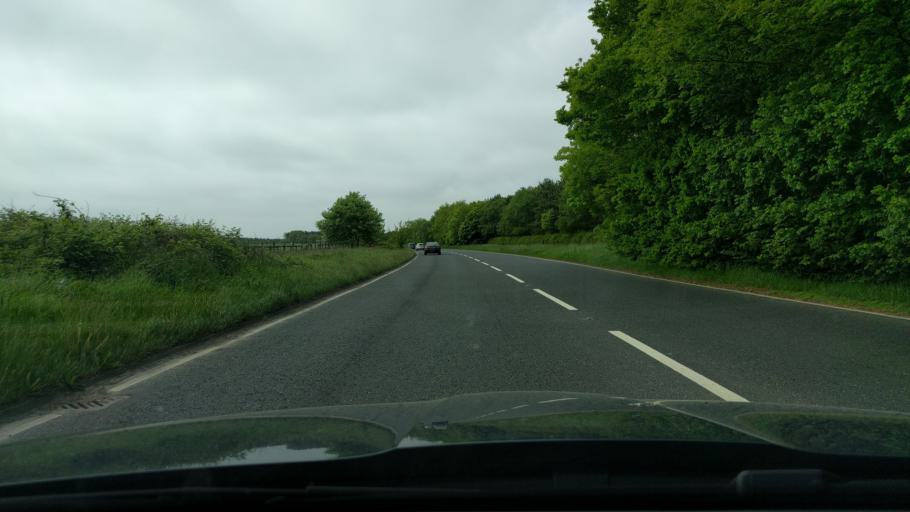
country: GB
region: England
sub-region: Northumberland
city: East Chevington
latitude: 55.2698
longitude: -1.6044
